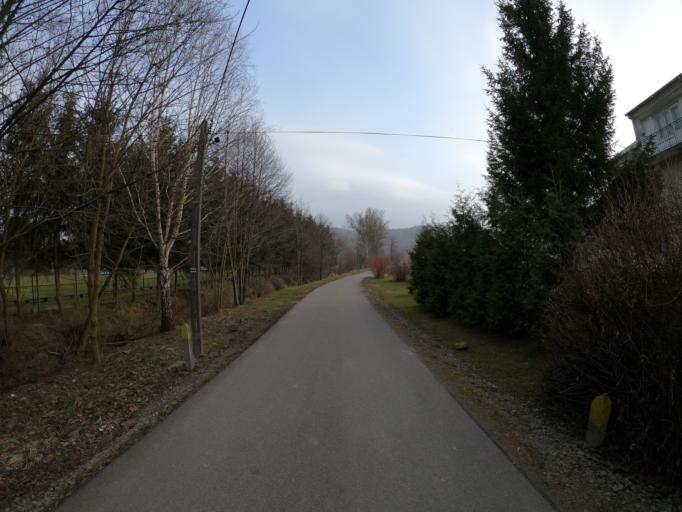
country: PL
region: Subcarpathian Voivodeship
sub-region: Powiat strzyzowski
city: Wisniowa
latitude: 49.8654
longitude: 21.6429
